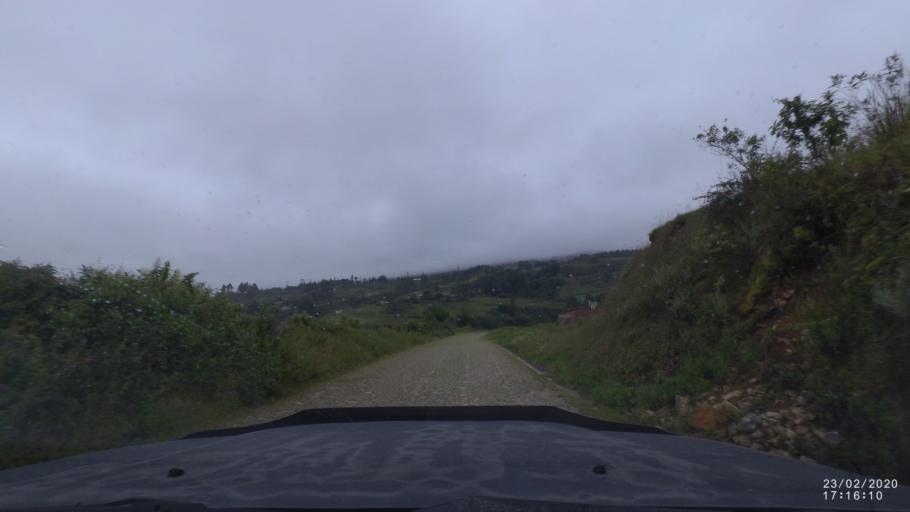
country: BO
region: Cochabamba
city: Colomi
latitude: -17.1336
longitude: -65.9388
